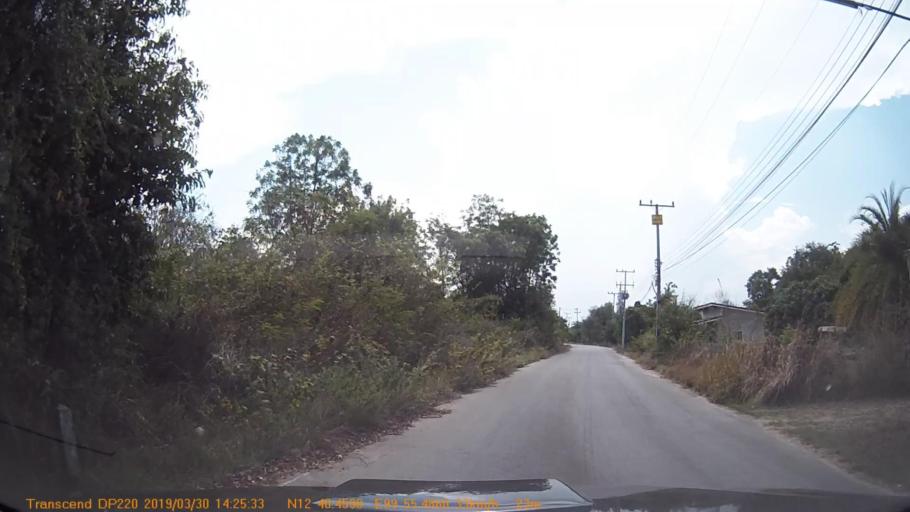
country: TH
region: Prachuap Khiri Khan
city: Hua Hin
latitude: 12.6744
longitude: 99.9246
